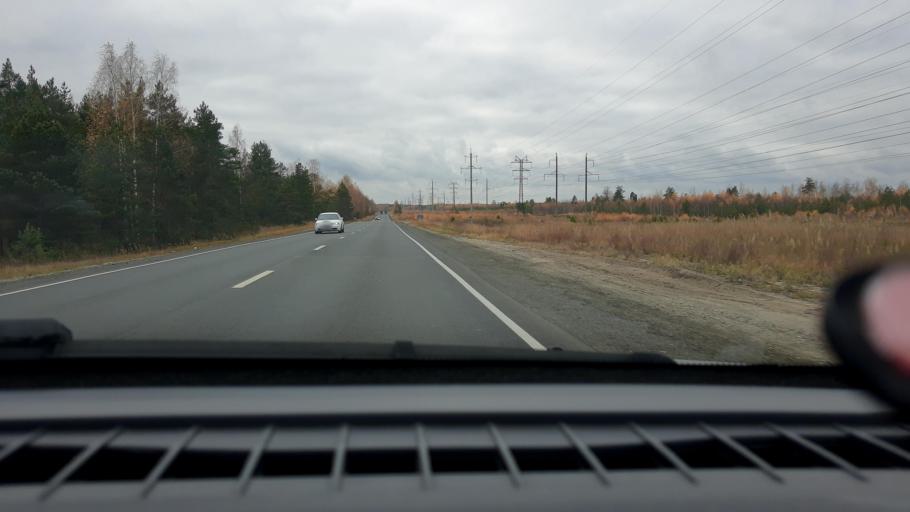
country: RU
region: Nizjnij Novgorod
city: Lukino
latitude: 56.3796
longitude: 43.6294
